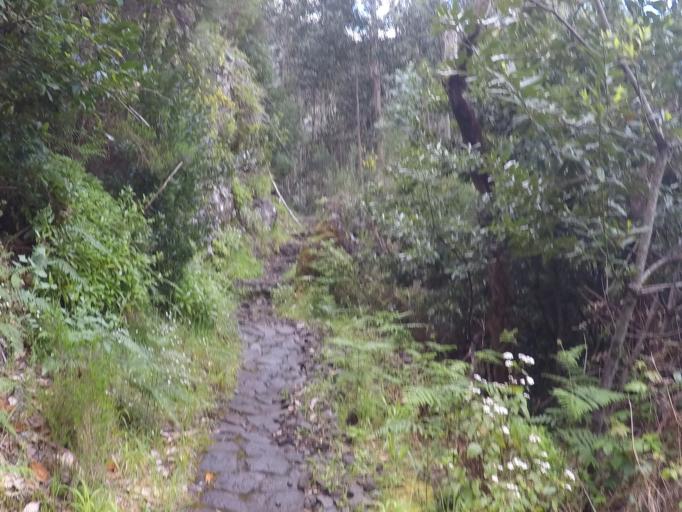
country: PT
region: Madeira
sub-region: Camara de Lobos
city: Curral das Freiras
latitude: 32.7474
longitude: -17.0050
